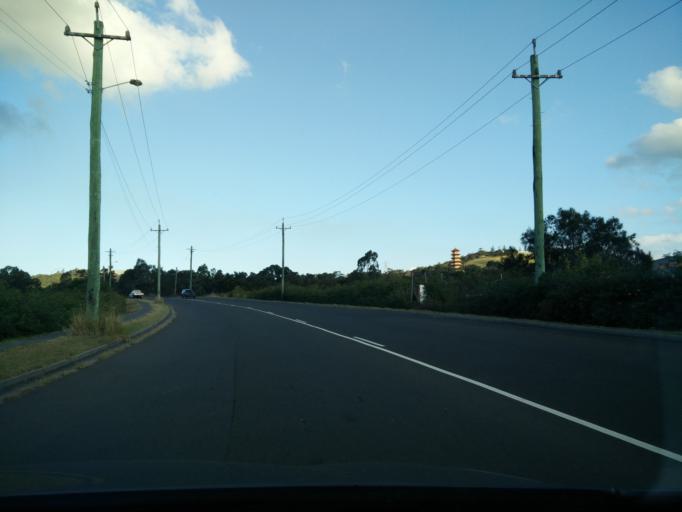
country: AU
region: New South Wales
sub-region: Wollongong
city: Berkeley
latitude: -34.4606
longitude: 150.8508
